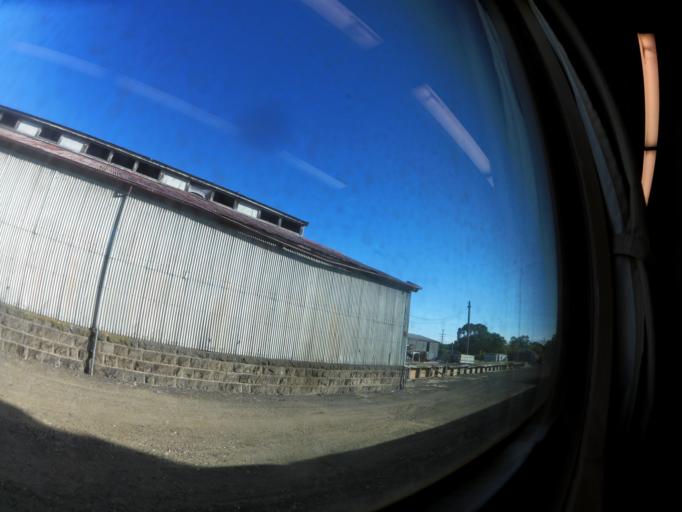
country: AU
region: Victoria
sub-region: Greater Shepparton
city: Shepparton
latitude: -36.7490
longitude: 145.5681
